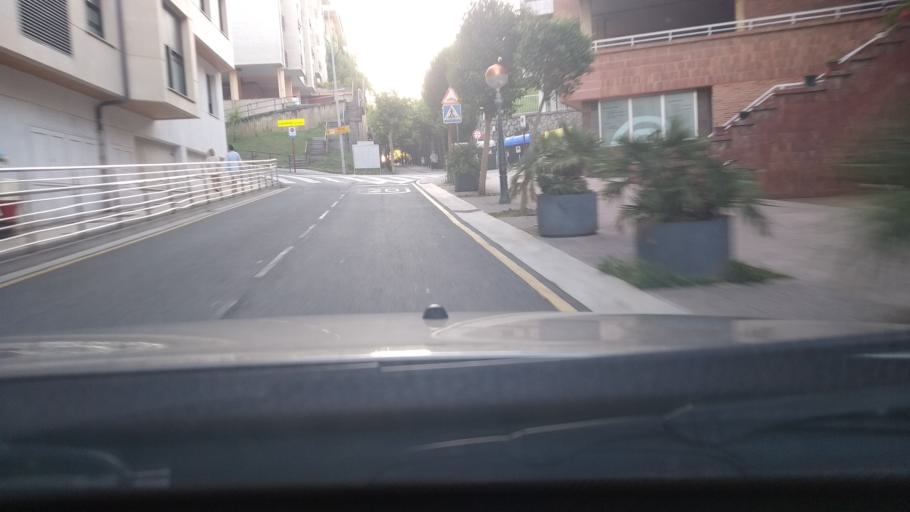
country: ES
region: Basque Country
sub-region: Provincia de Guipuzcoa
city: Zumaia
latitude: 43.2985
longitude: -2.2568
